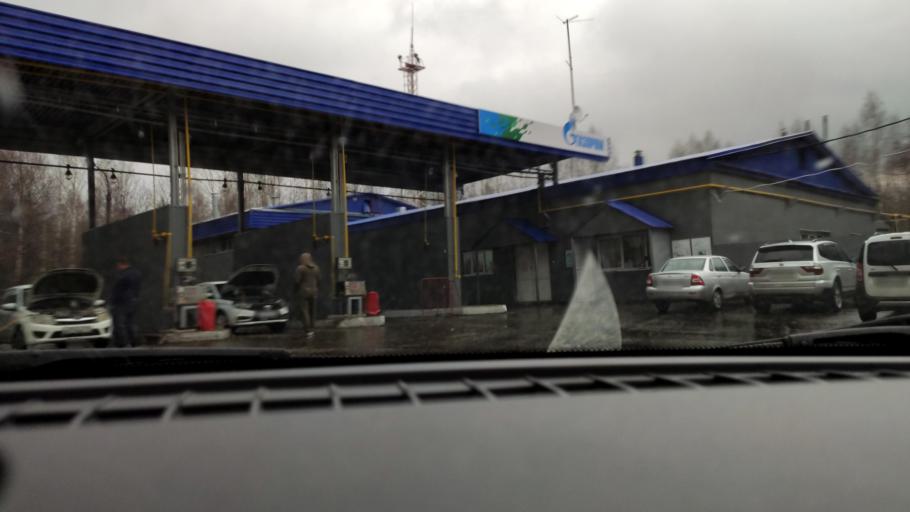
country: RU
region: Perm
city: Perm
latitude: 58.1076
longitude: 56.3974
